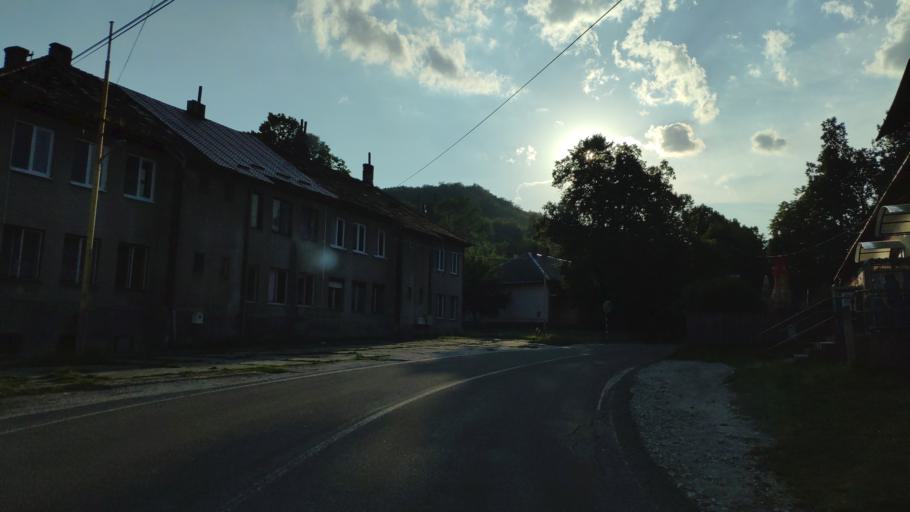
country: SK
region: Kosicky
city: Dobsina
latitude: 48.7179
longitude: 20.2700
